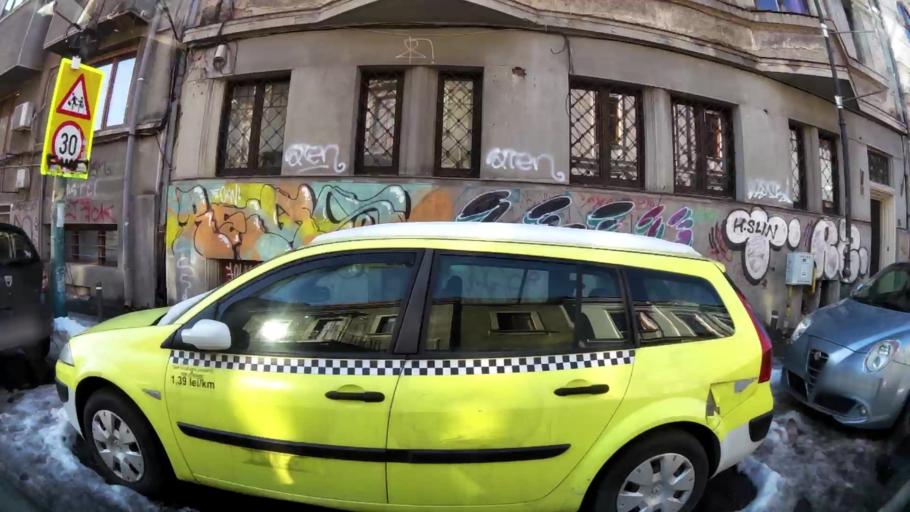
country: RO
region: Bucuresti
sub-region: Municipiul Bucuresti
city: Bucharest
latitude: 44.4416
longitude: 26.1021
